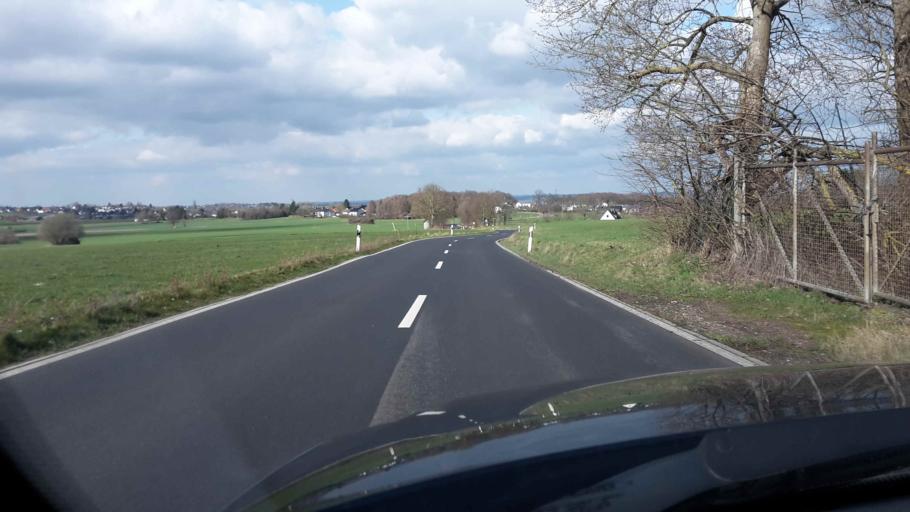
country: DE
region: North Rhine-Westphalia
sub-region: Regierungsbezirk Koln
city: Hennef
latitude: 50.7165
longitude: 7.3147
